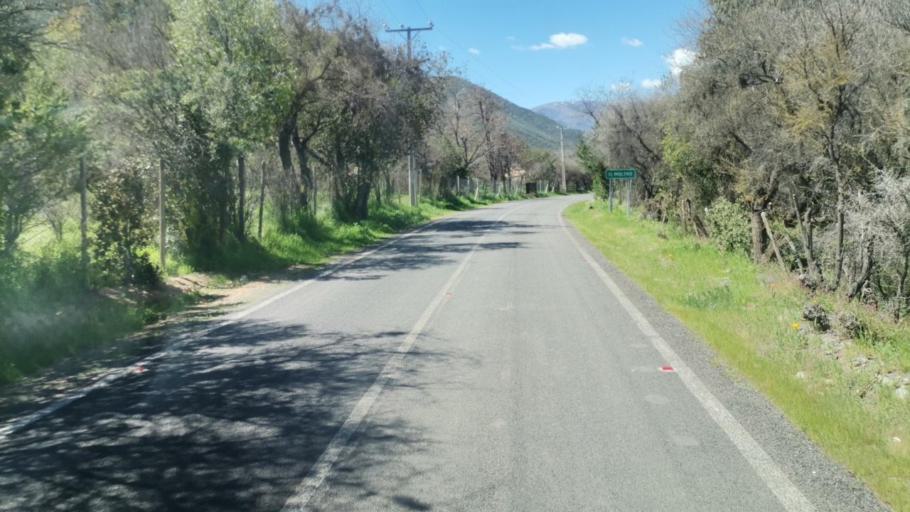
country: CL
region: Valparaiso
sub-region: Provincia de Marga Marga
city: Limache
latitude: -33.1686
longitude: -71.1492
